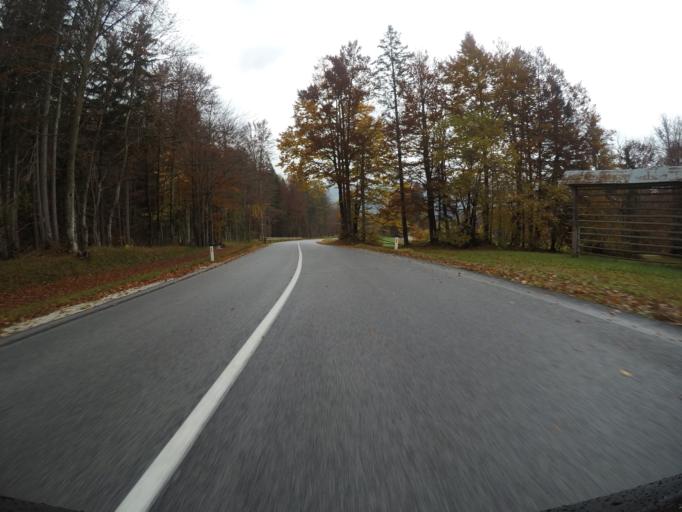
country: SI
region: Kranjska Gora
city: Kranjska Gora
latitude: 46.4806
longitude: 13.7231
